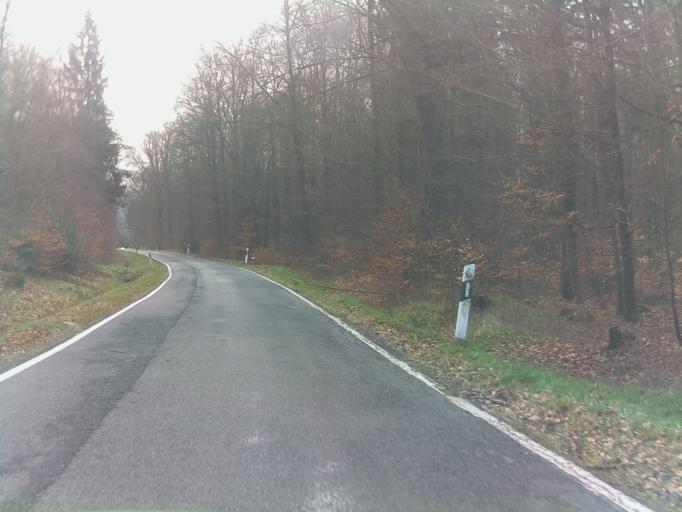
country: DE
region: Rheinland-Pfalz
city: Ippenschied
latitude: 49.8911
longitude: 7.6220
